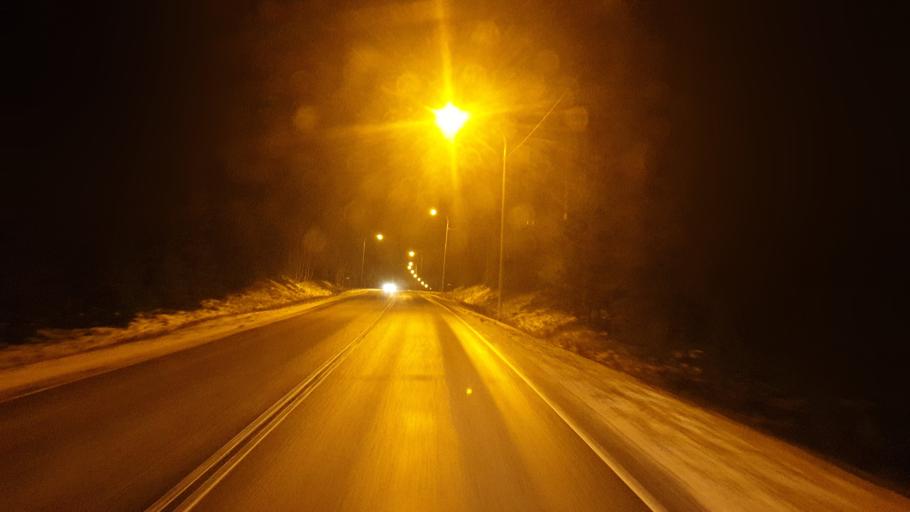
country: FI
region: Southern Savonia
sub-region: Pieksaemaeki
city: Jaeppilae
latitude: 62.6809
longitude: 27.4463
